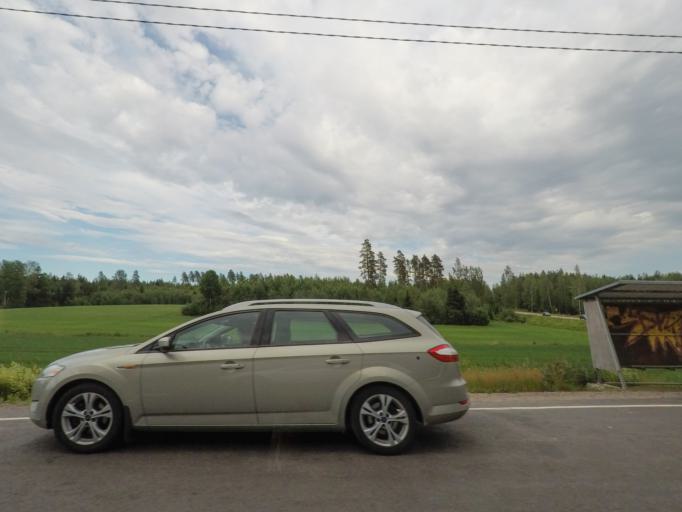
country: FI
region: Uusimaa
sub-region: Porvoo
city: Pukkila
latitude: 60.7728
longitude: 25.4516
